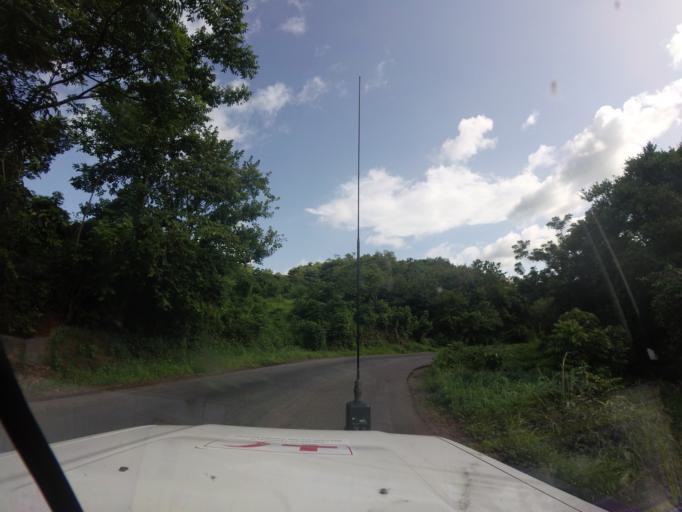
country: GN
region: Mamou
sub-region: Mamou Prefecture
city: Mamou
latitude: 10.2157
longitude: -12.4603
